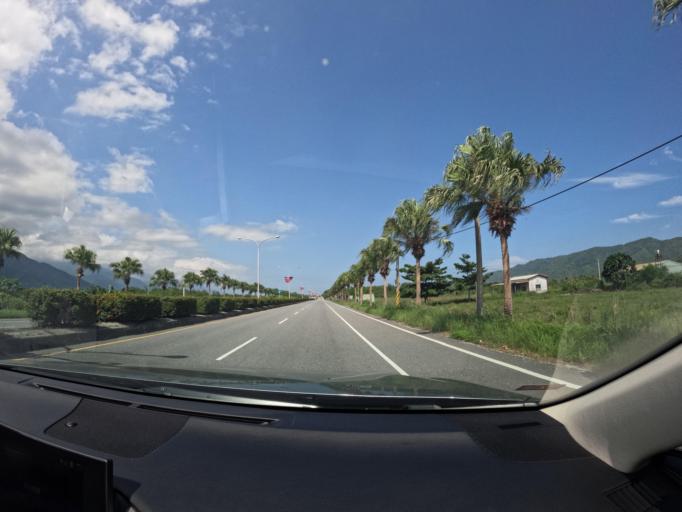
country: TW
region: Taiwan
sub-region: Hualien
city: Hualian
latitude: 23.8750
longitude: 121.5387
